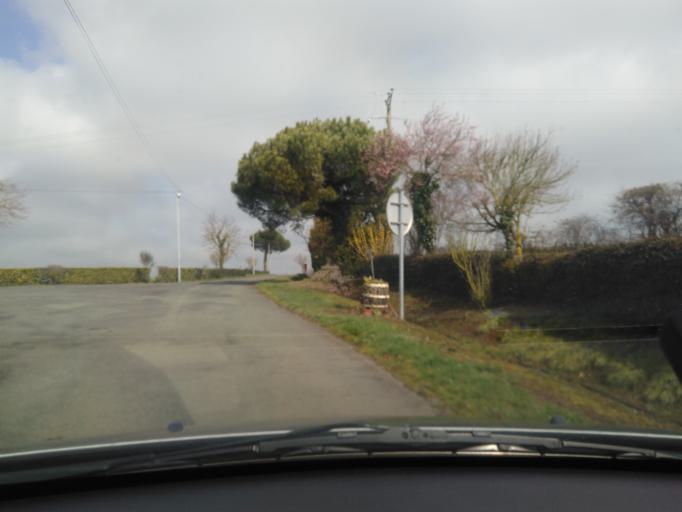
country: FR
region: Pays de la Loire
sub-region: Departement de la Vendee
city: Sainte-Cecile
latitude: 46.7051
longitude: -1.1356
